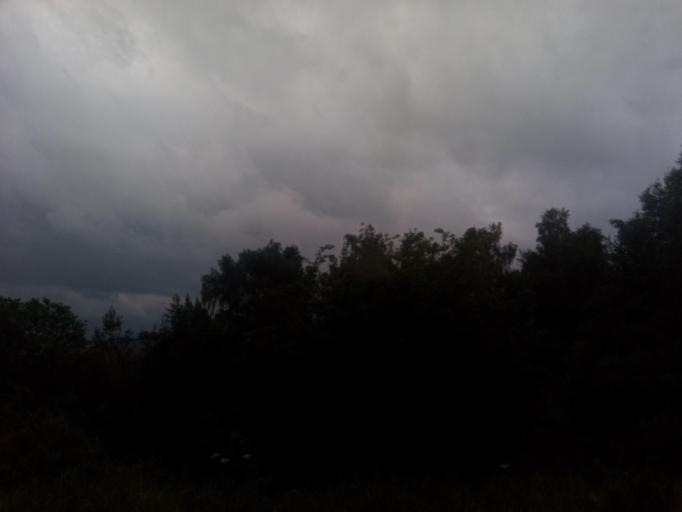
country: GB
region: England
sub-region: North Yorkshire
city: Settle
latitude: 54.0085
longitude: -2.2231
